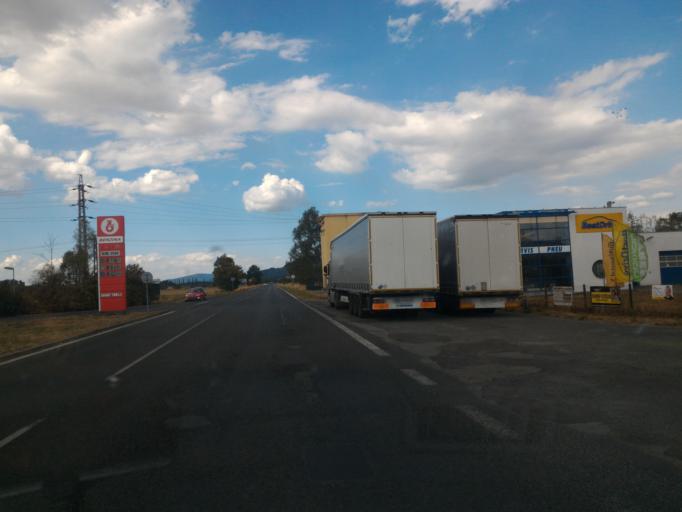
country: CZ
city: Mimon
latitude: 50.6679
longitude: 14.7270
